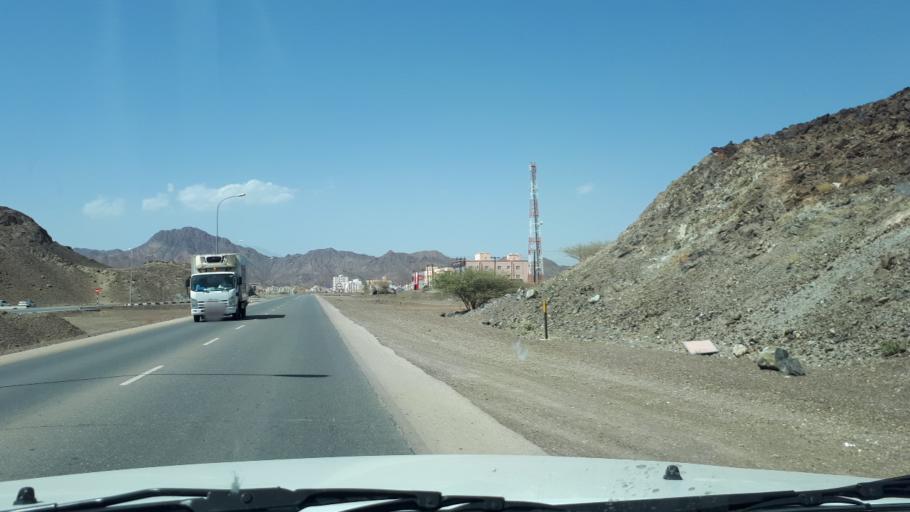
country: OM
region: Muhafazat ad Dakhiliyah
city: Bahla'
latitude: 22.9361
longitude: 57.2582
